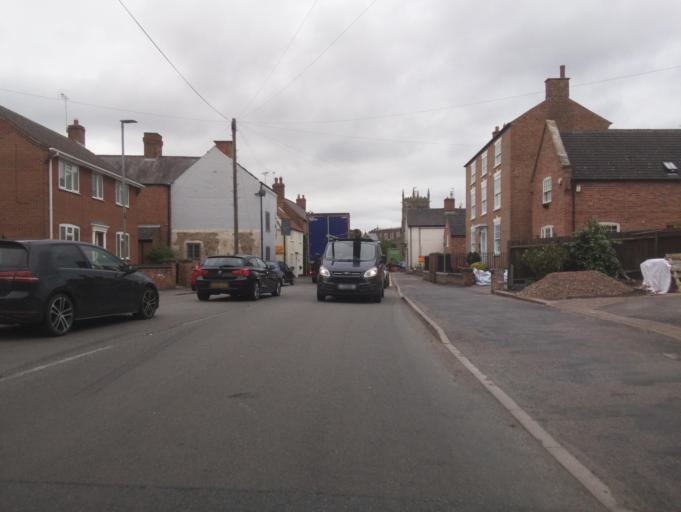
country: GB
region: England
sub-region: Leicestershire
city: Barrow upon Soar
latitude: 52.8063
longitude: -1.1091
